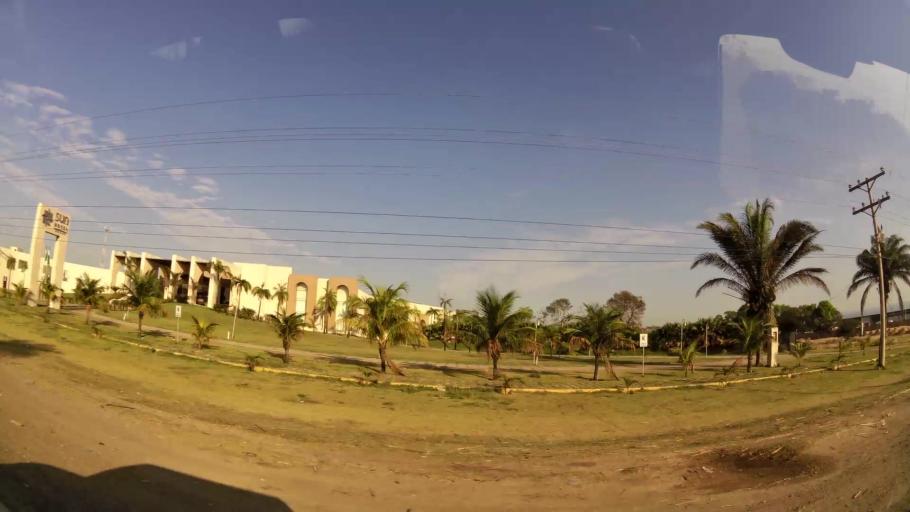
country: BO
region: Santa Cruz
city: La Belgica
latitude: -17.6561
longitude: -63.1580
